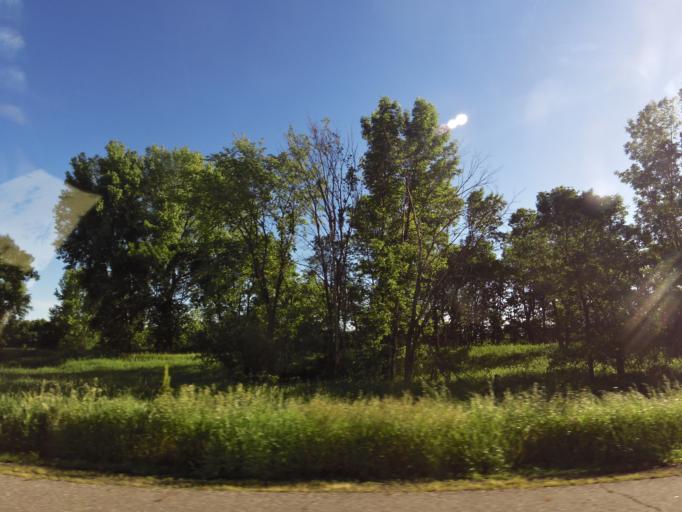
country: US
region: Minnesota
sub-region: Stearns County
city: Albany
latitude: 45.6391
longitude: -94.6232
